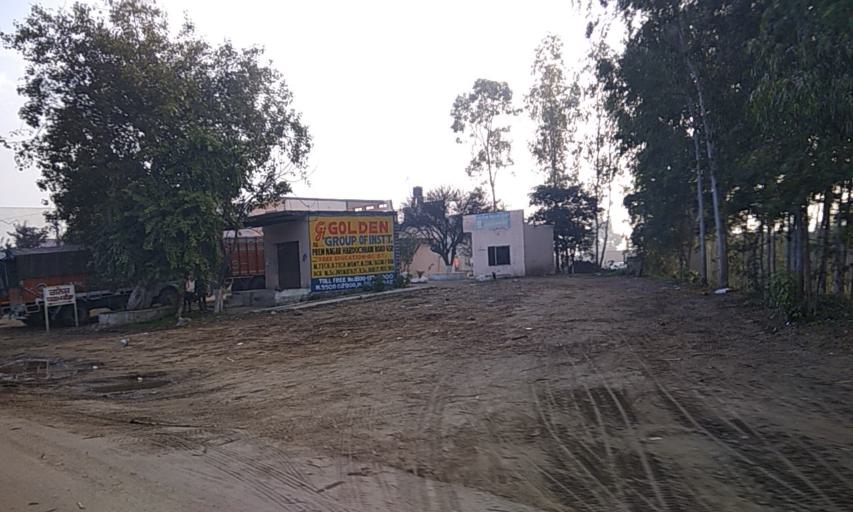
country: IN
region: Punjab
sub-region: Gurdaspur
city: Dhariwal
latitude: 31.9409
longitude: 75.3114
